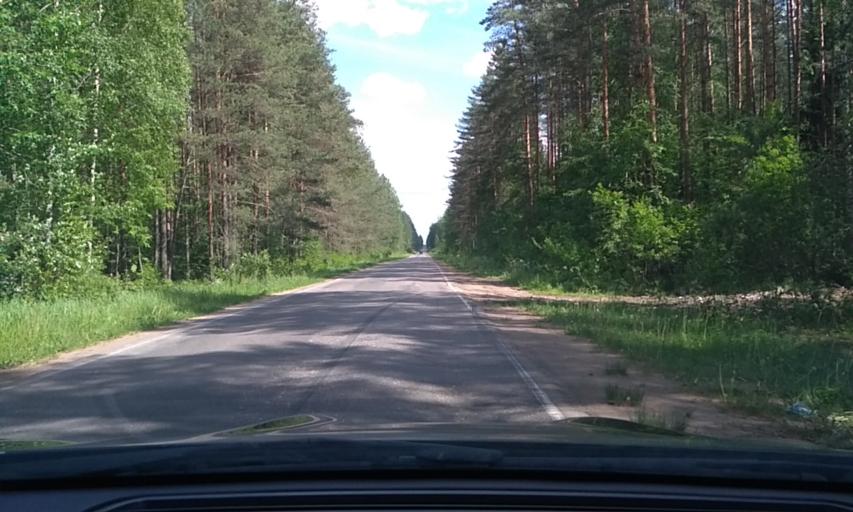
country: RU
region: Leningrad
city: Imeni Sverdlova
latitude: 59.8236
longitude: 30.7267
